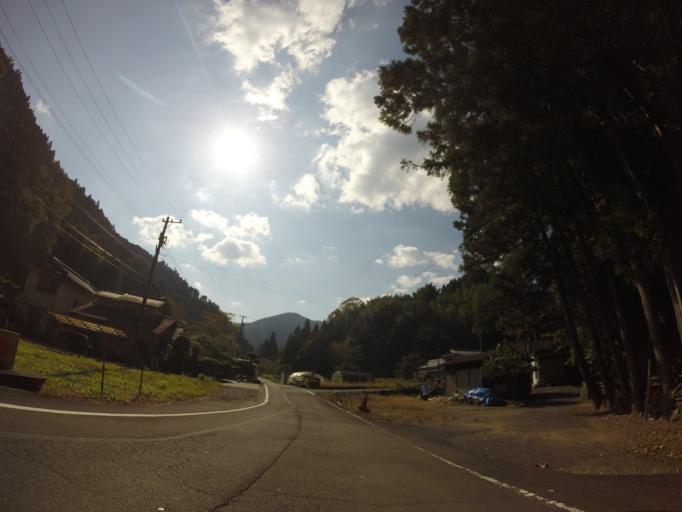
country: JP
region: Shizuoka
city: Shizuoka-shi
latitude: 35.1145
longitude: 138.4516
